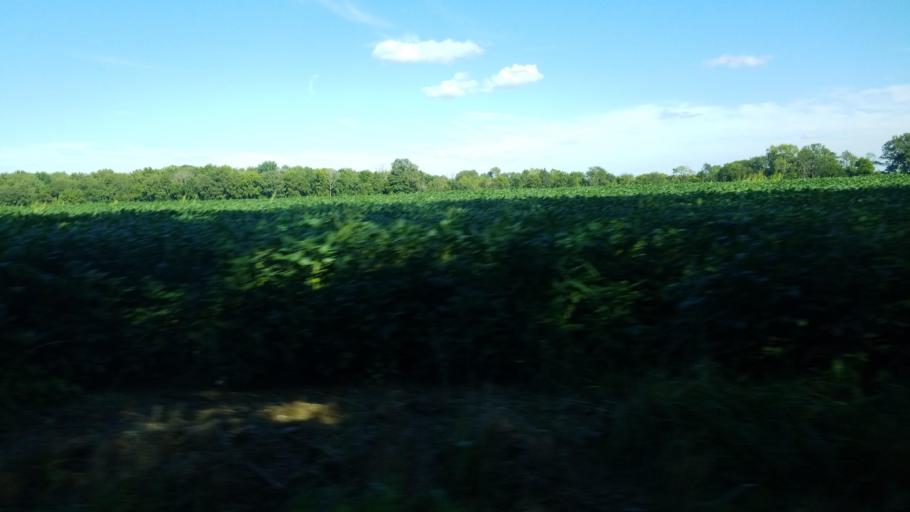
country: US
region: Illinois
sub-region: Saline County
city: Harrisburg
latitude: 37.8161
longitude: -88.5672
